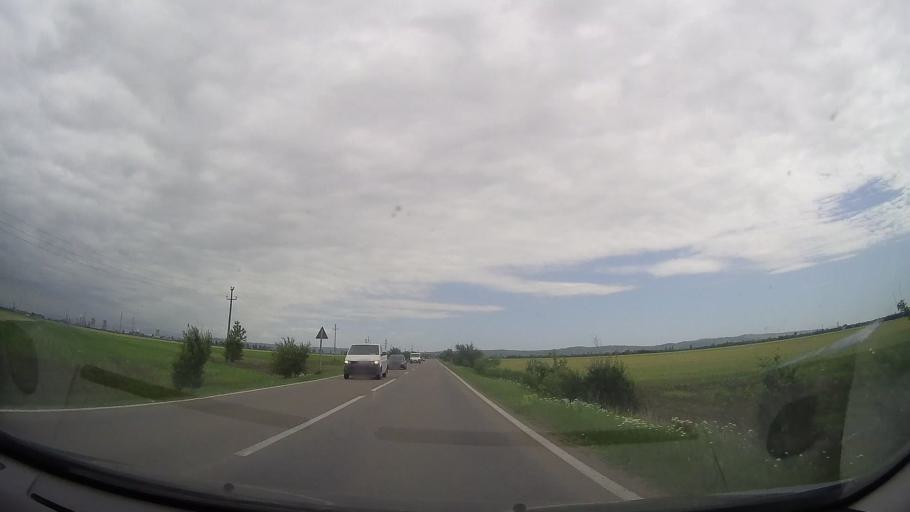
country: RO
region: Prahova
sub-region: Comuna Berceni
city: Corlatesti
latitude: 44.9204
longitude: 26.1018
